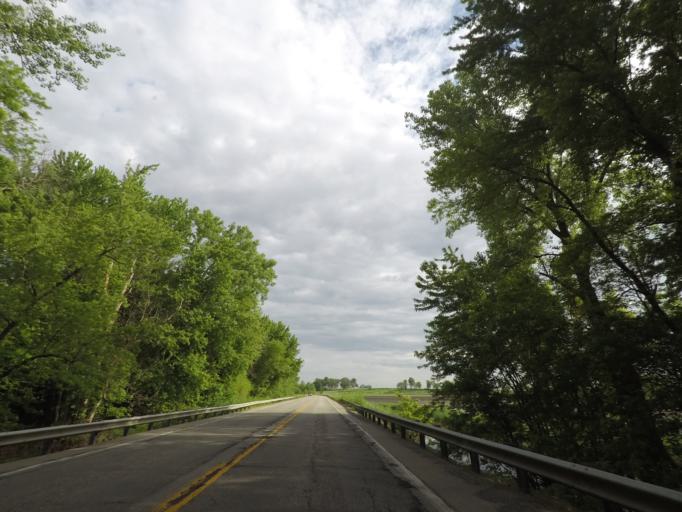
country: US
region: Illinois
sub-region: Logan County
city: Mount Pulaski
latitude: 40.0564
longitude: -89.2820
